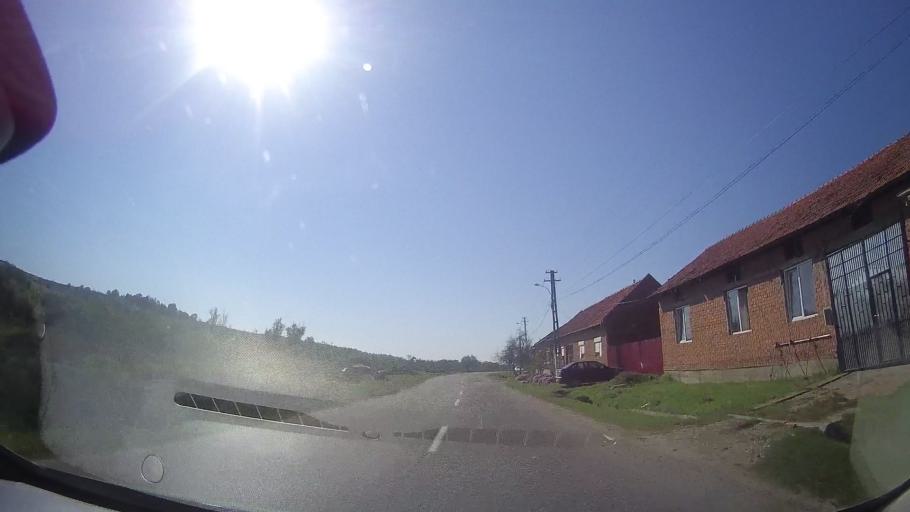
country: RO
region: Timis
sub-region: Comuna Ohaba Lunga
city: Ohaba Lunga
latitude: 45.9038
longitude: 21.9800
